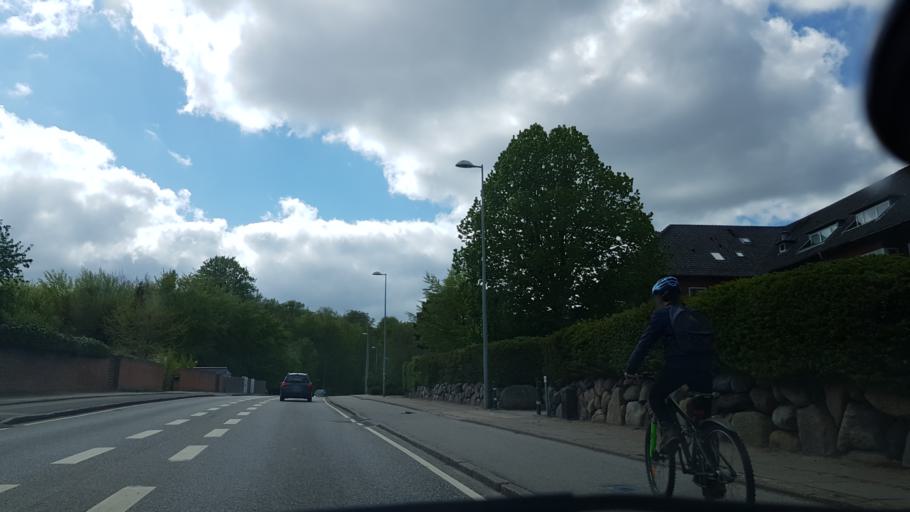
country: DK
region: Capital Region
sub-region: Horsholm Kommune
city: Horsholm
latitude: 55.8835
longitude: 12.5271
